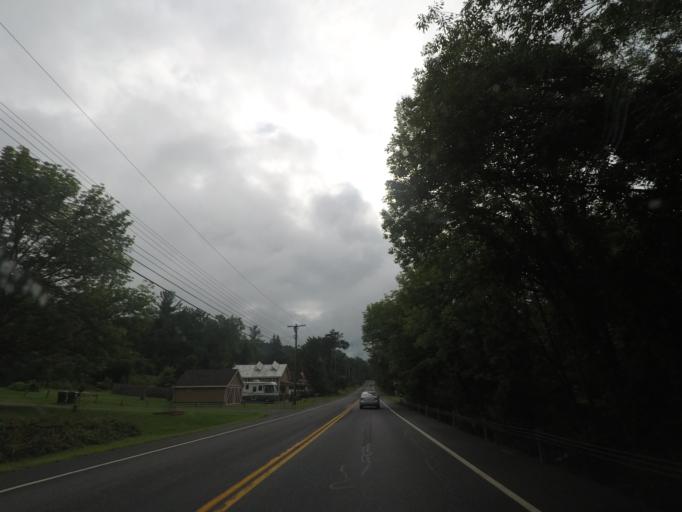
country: US
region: New York
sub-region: Rensselaer County
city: Nassau
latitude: 42.4957
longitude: -73.5180
